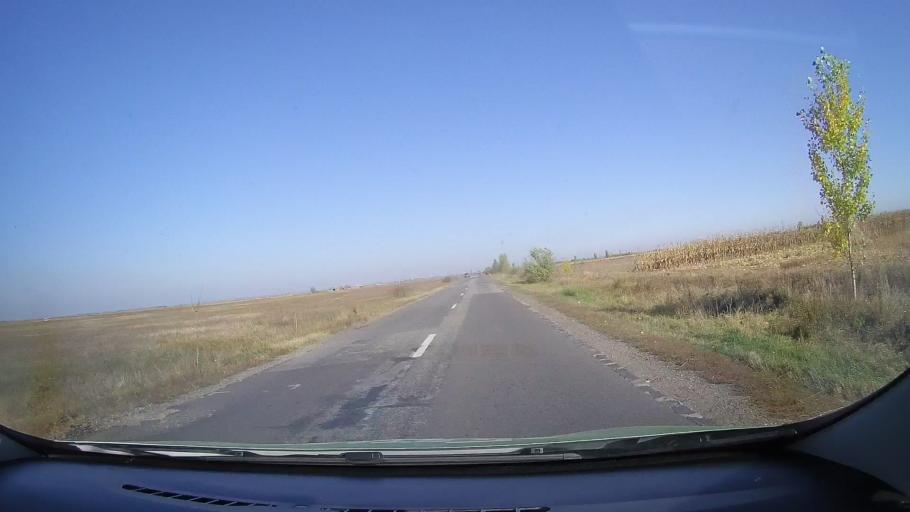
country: RO
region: Satu Mare
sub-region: Comuna Cauas
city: Cauas
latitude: 47.5292
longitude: 22.5673
